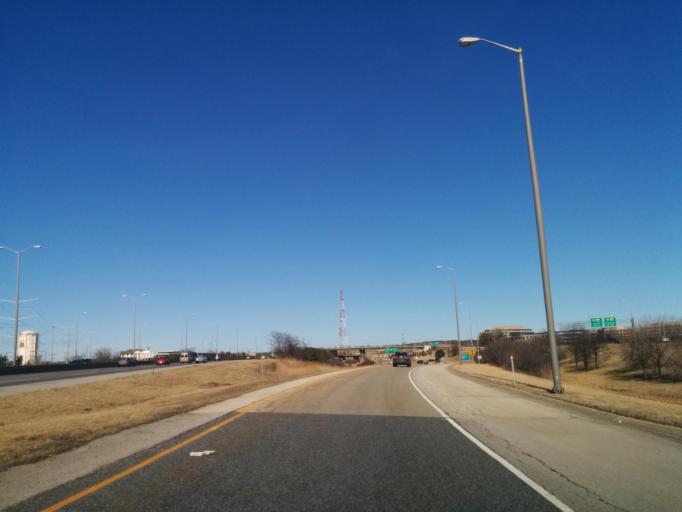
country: US
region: Illinois
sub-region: DuPage County
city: Lisle
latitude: 41.8007
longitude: -88.0563
